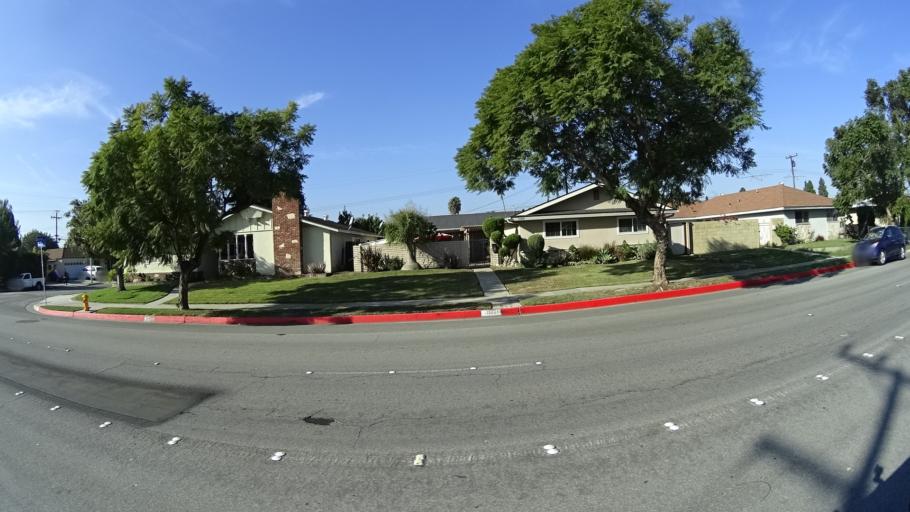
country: US
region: California
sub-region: Orange County
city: Midway City
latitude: 33.7182
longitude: -117.9807
